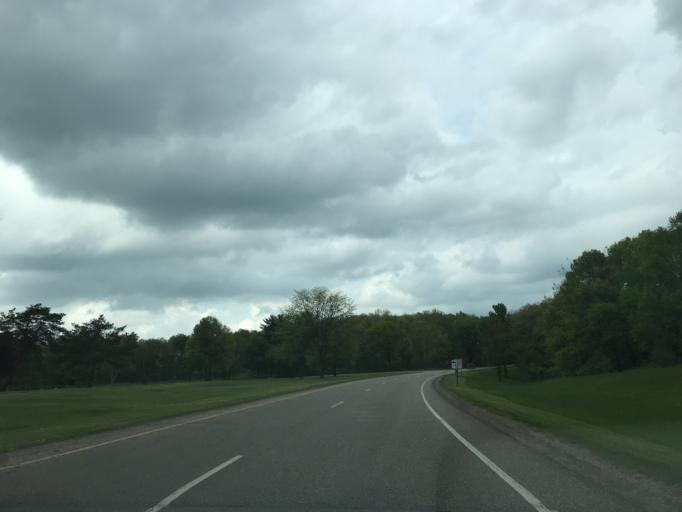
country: US
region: Michigan
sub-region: Oakland County
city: Milford
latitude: 42.5471
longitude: -83.6285
